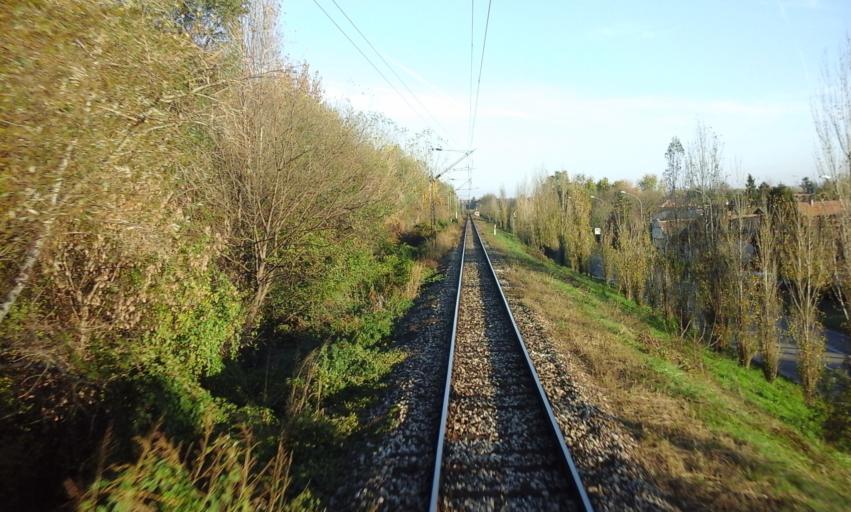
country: RS
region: Autonomna Pokrajina Vojvodina
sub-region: Juznobacki Okrug
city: Petrovaradin
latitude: 45.2579
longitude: 19.8701
